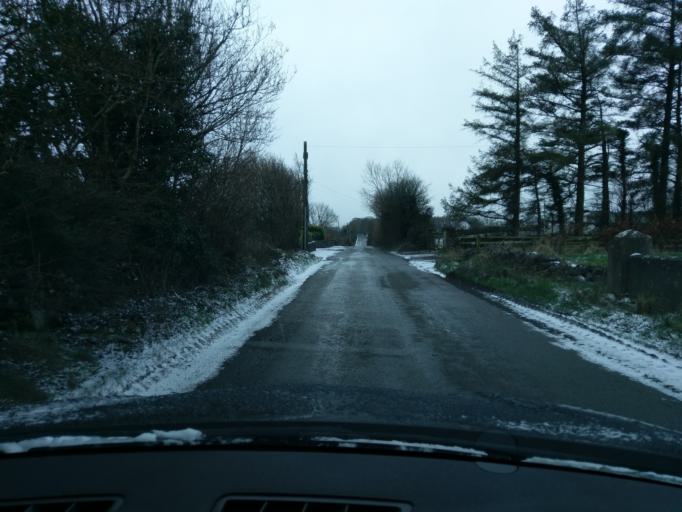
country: IE
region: Connaught
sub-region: County Galway
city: Athenry
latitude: 53.2732
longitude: -8.8111
